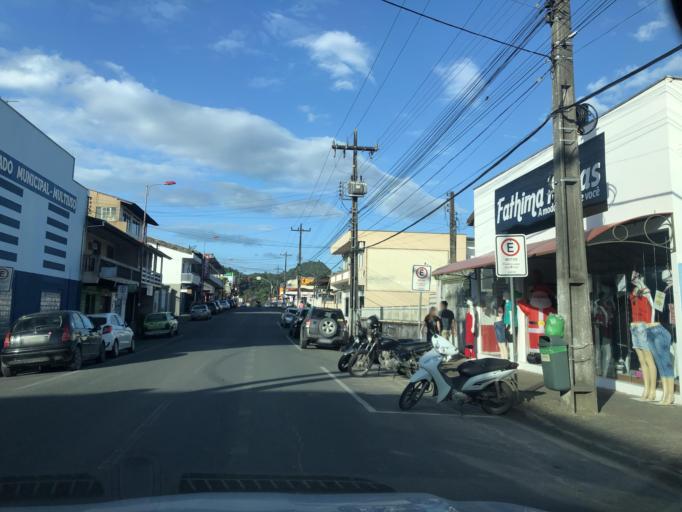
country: BR
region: Santa Catarina
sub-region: Sao Francisco Do Sul
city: Sao Francisco do Sul
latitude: -26.2503
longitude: -48.6362
